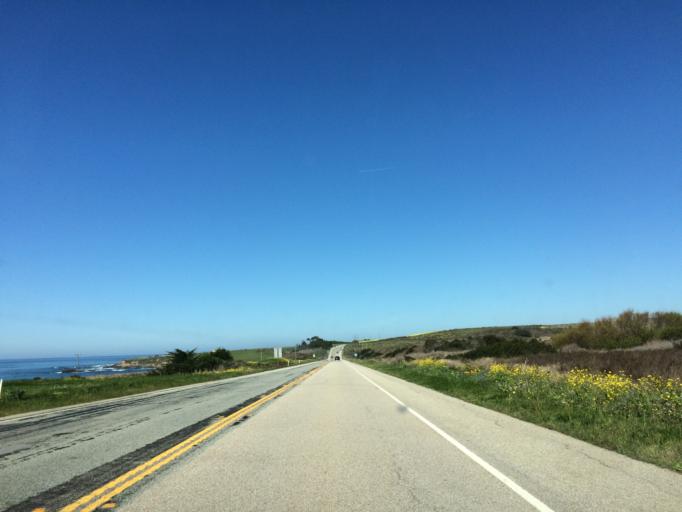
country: US
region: California
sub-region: San Mateo County
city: Portola Valley
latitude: 37.1891
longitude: -122.3946
